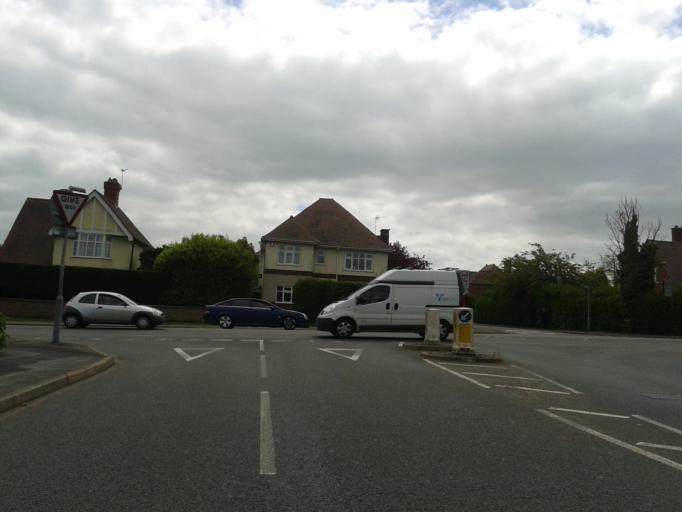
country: GB
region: England
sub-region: Leicestershire
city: Hinckley
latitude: 52.5505
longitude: -1.3568
